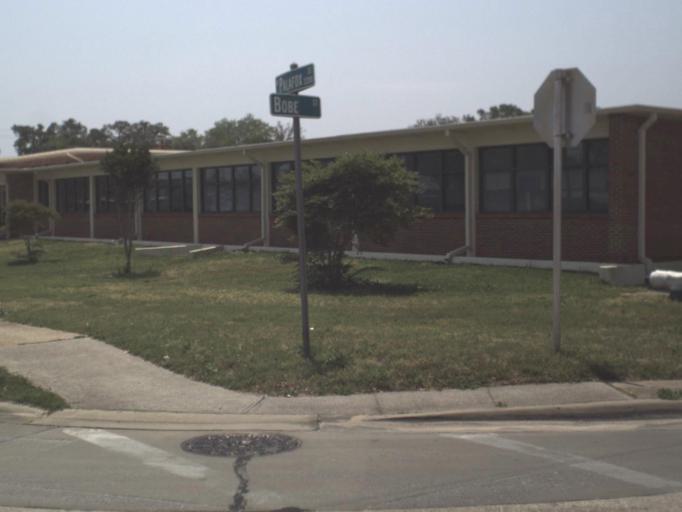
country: US
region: Florida
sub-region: Escambia County
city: Goulding
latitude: 30.4355
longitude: -87.2207
